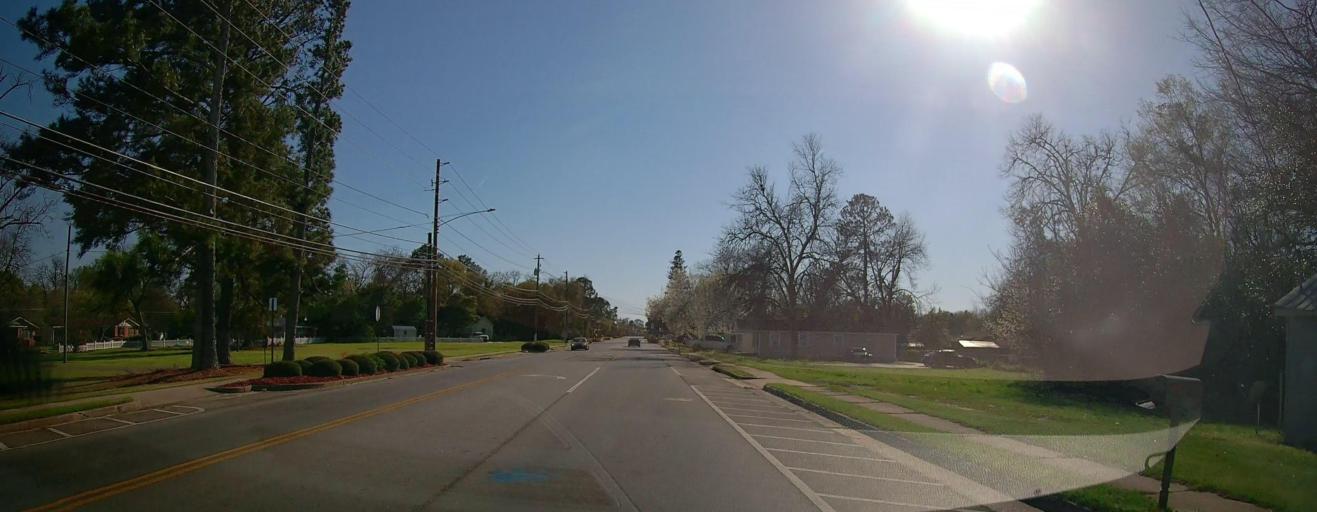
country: US
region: Georgia
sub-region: Peach County
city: Fort Valley
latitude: 32.5451
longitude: -83.8924
